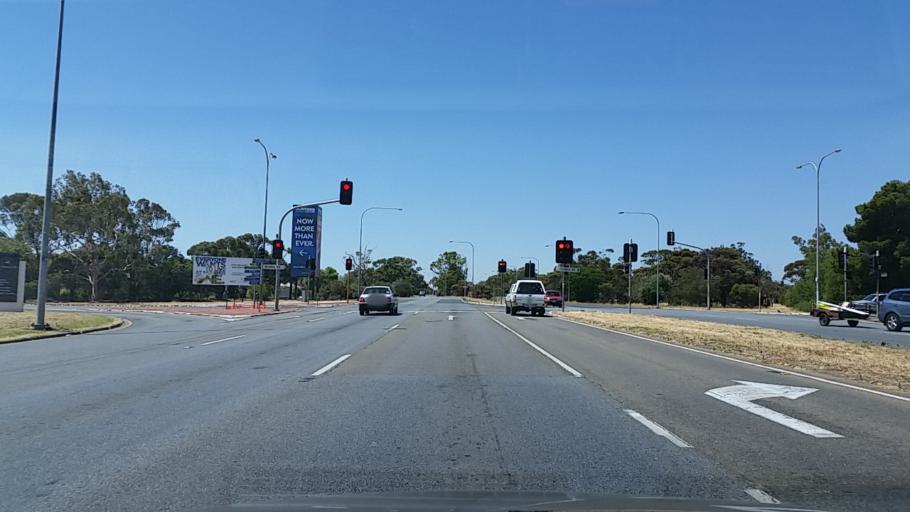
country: AU
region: South Australia
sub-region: Salisbury
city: Elizabeth
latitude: -34.7077
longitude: 138.6782
